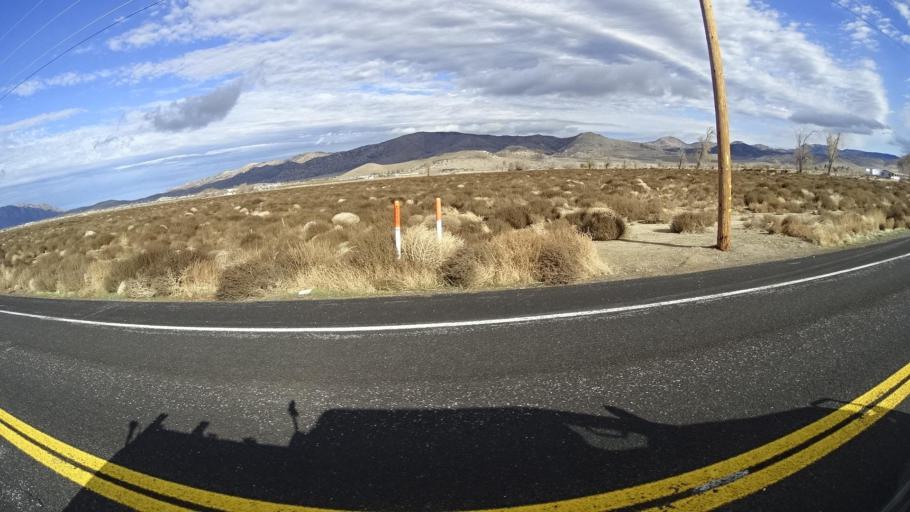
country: US
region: California
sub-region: Kern County
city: Tehachapi
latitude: 35.1097
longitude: -118.4113
